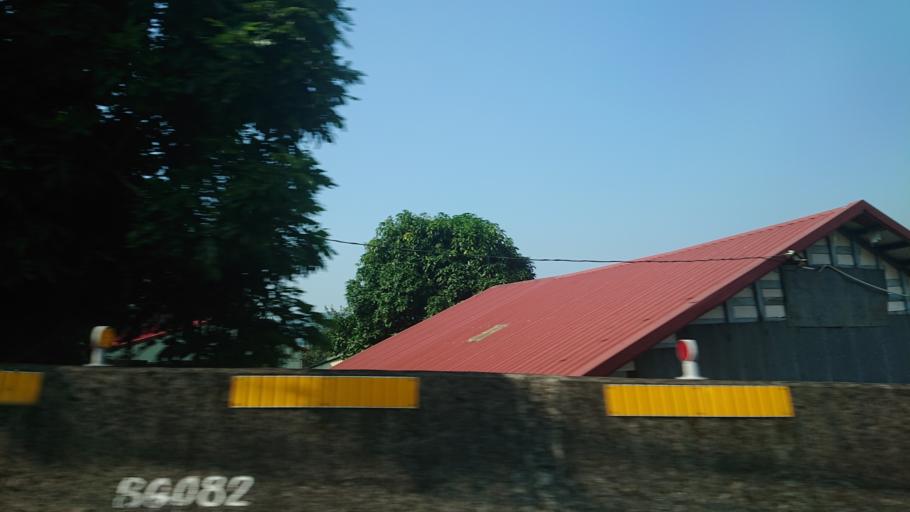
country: TW
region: Taiwan
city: Lugu
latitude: 23.6922
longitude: 120.6634
